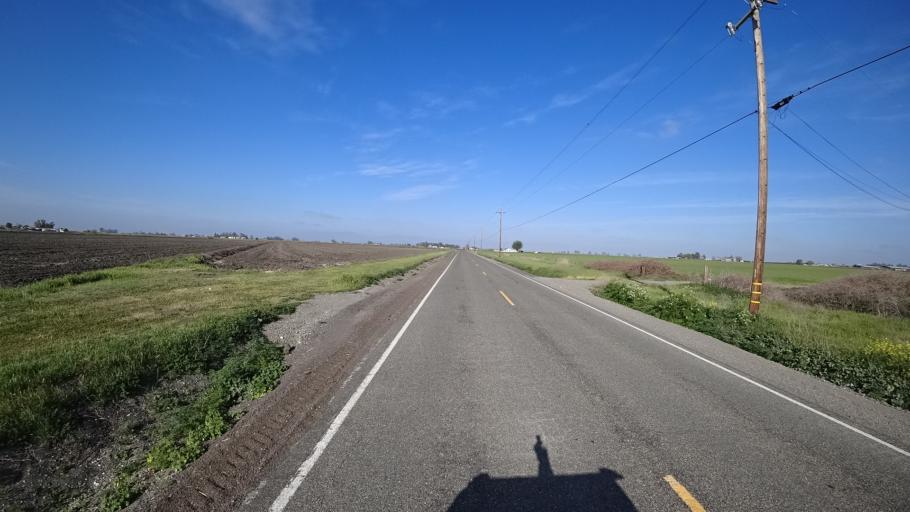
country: US
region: California
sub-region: Glenn County
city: Willows
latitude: 39.5828
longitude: -122.0791
